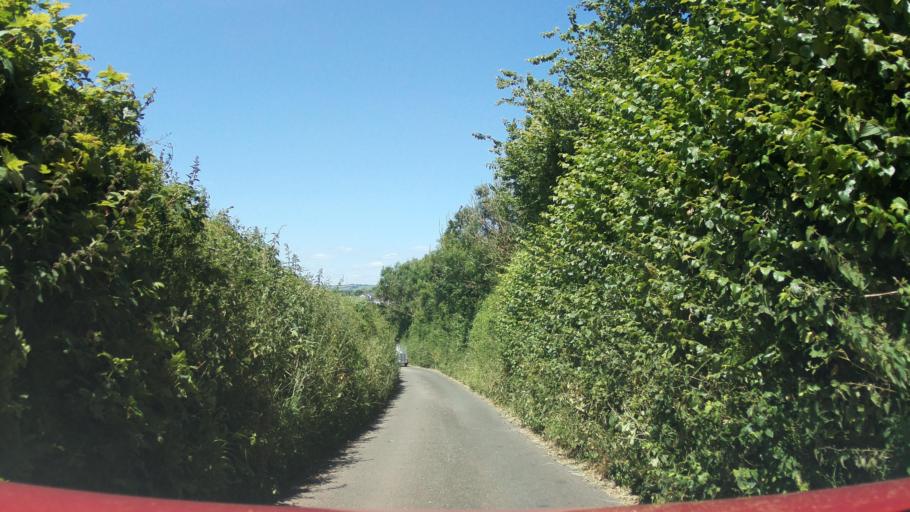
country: GB
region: England
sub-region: Devon
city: Dartmouth
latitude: 50.3909
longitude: -3.5634
